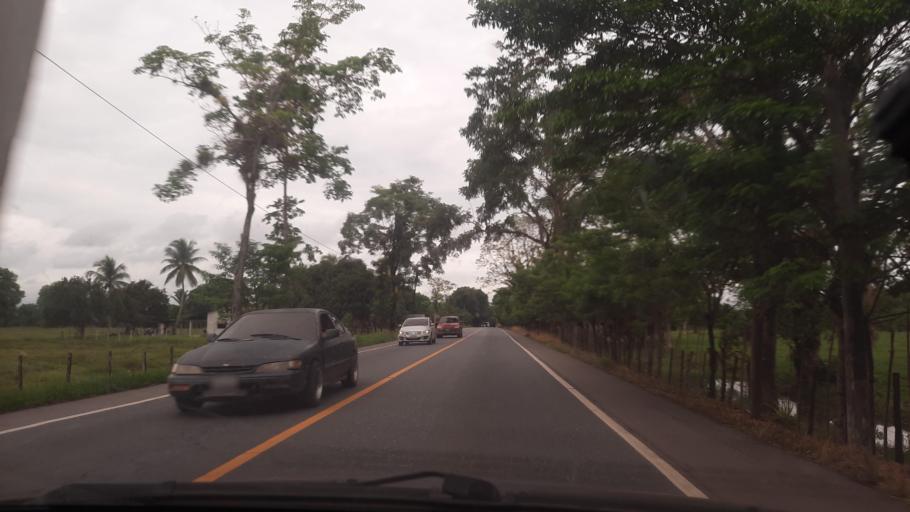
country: GT
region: Izabal
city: Morales
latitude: 15.4554
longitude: -88.9347
